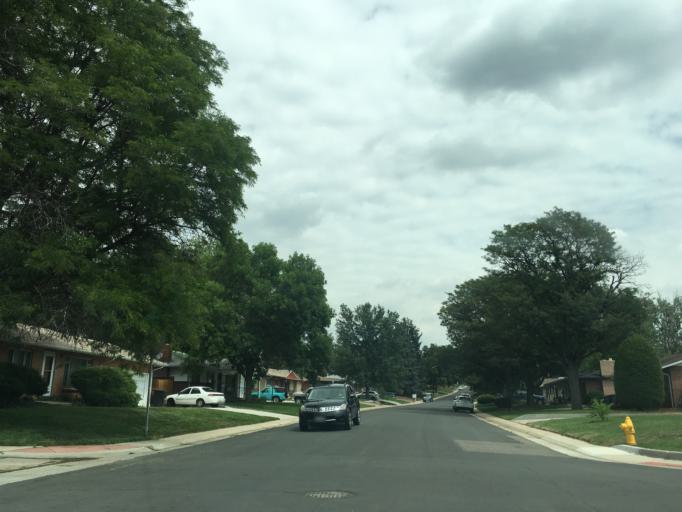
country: US
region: Colorado
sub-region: Arapahoe County
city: Sheridan
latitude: 39.6596
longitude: -105.0520
